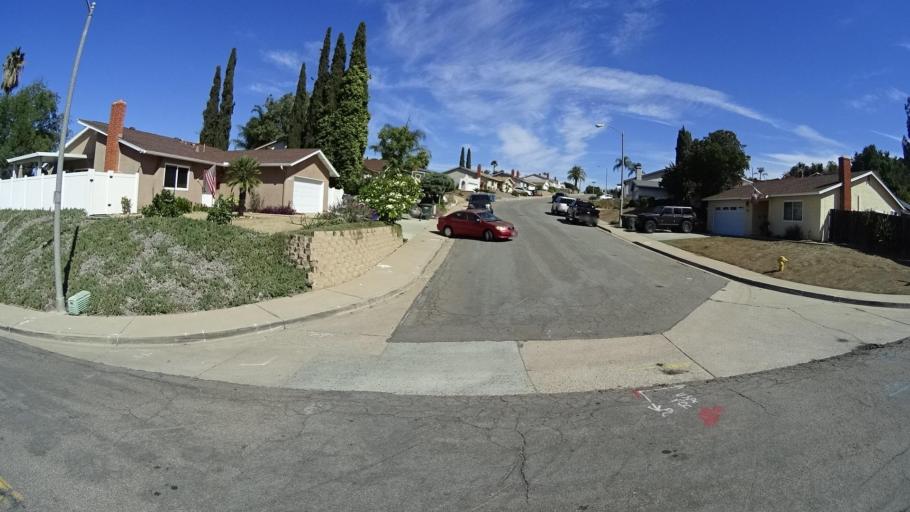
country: US
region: California
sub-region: San Diego County
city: Granite Hills
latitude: 32.8307
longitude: -116.8943
